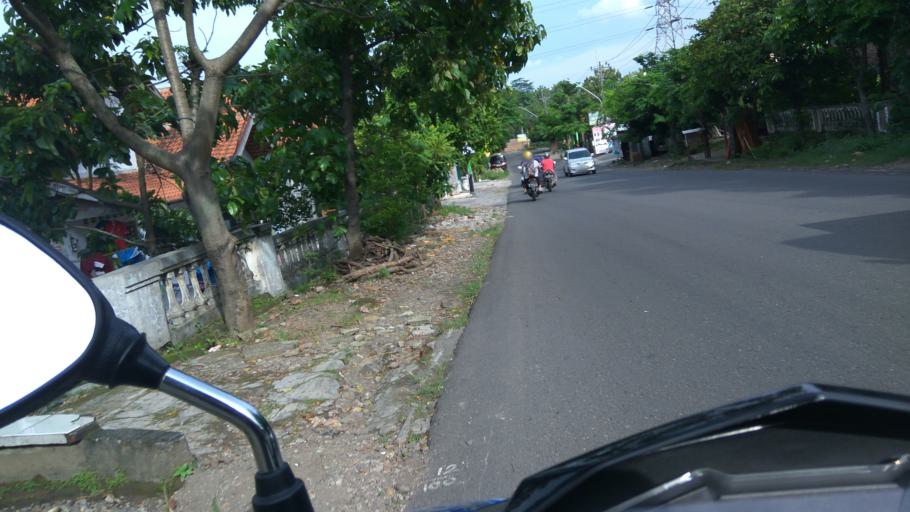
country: ID
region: Central Java
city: Mranggen
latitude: -7.0457
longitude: 110.4616
